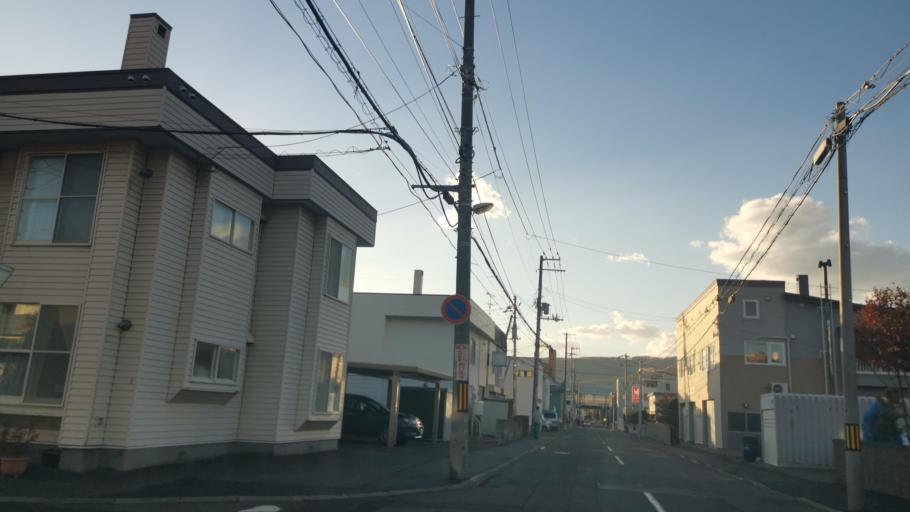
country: JP
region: Hokkaido
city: Sapporo
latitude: 43.0095
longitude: 141.3690
